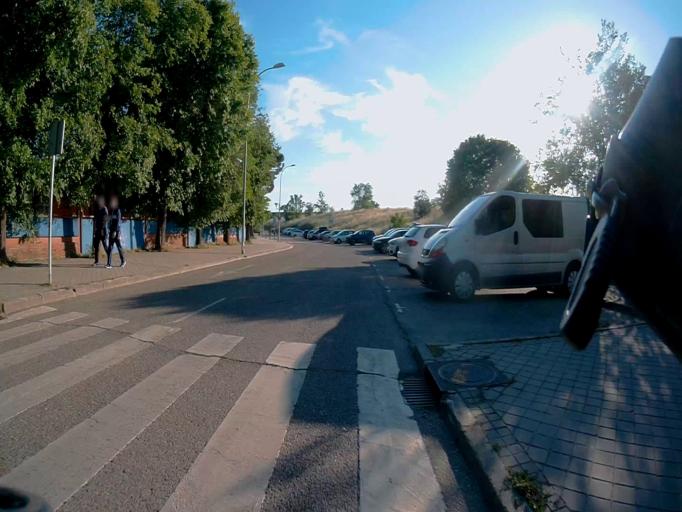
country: ES
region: Madrid
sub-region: Provincia de Madrid
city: Alcorcon
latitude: 40.3367
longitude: -3.8450
